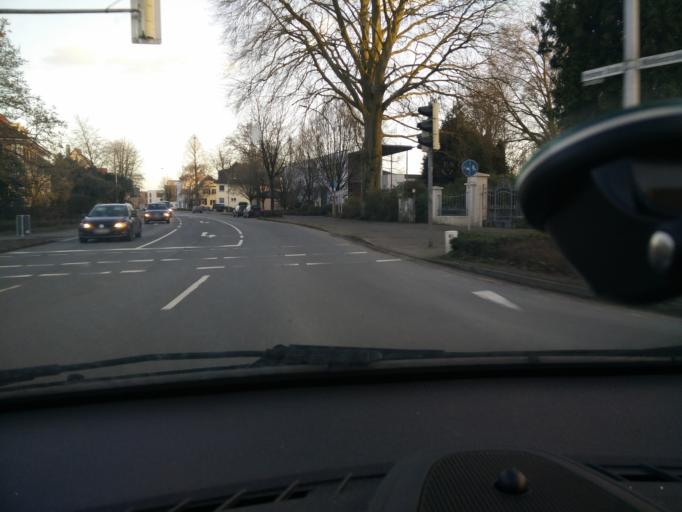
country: DE
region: North Rhine-Westphalia
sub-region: Regierungsbezirk Munster
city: Borken
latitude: 51.8442
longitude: 6.8637
